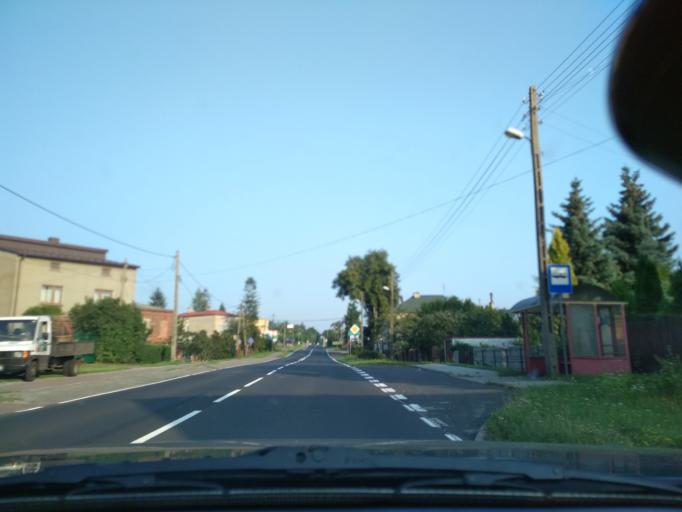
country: PL
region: Silesian Voivodeship
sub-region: Powiat zawiercianski
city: Ogrodzieniec
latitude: 50.4673
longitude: 19.4876
